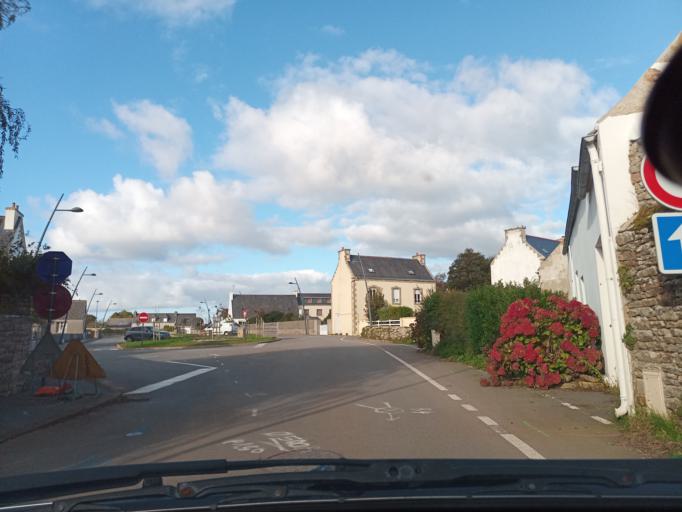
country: FR
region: Brittany
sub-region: Departement du Finistere
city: Plouhinec
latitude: 48.0133
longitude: -4.4887
